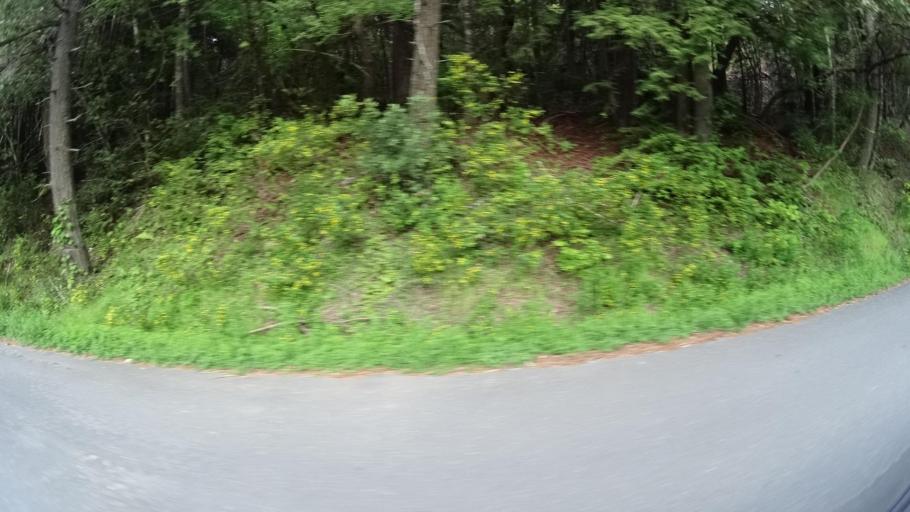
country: US
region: California
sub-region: Humboldt County
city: Redway
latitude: 40.2875
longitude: -123.8363
